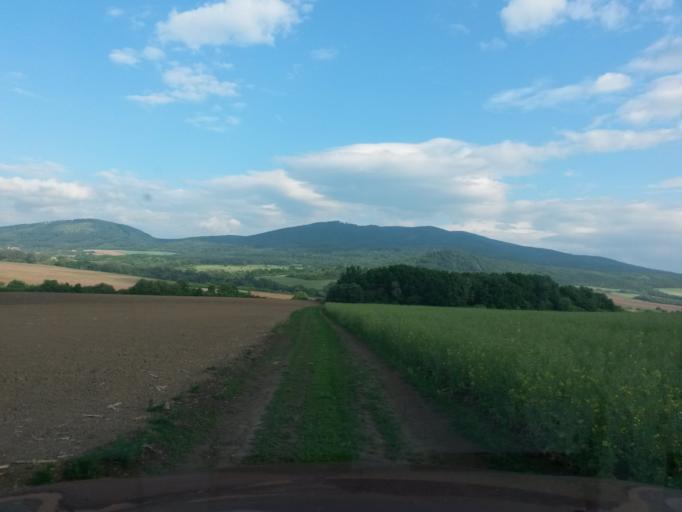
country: SK
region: Kosicky
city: Secovce
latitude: 48.7448
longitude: 21.4647
